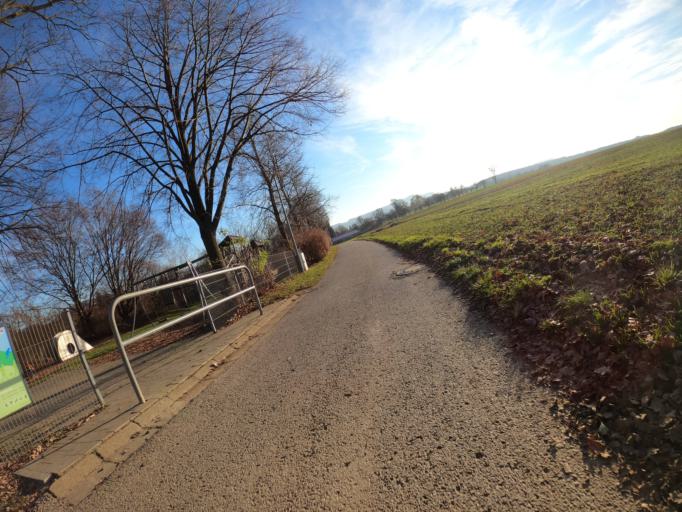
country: DE
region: Baden-Wuerttemberg
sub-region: Regierungsbezirk Stuttgart
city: Boll
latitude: 48.6686
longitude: 9.6126
